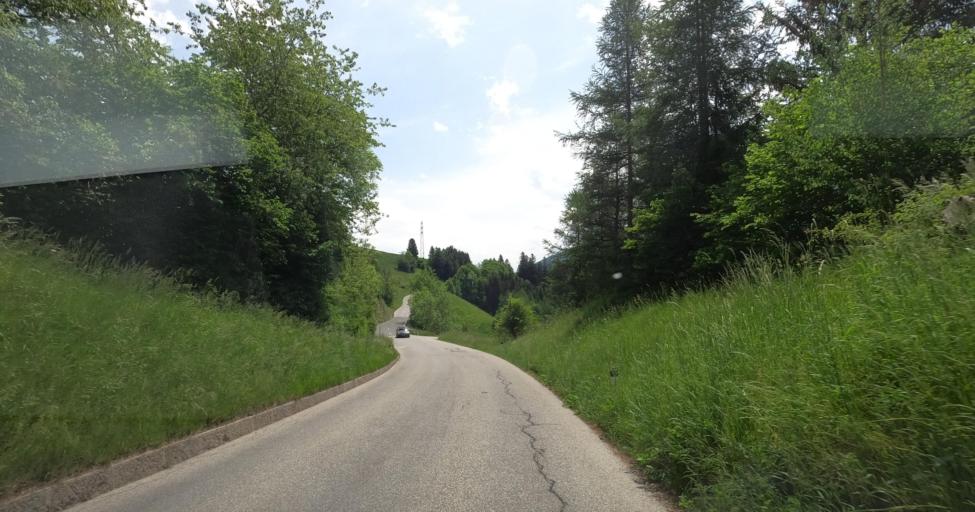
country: AT
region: Tyrol
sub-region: Politischer Bezirk Innsbruck Land
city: Schoenberg im Stubaital
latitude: 47.1903
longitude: 11.4277
